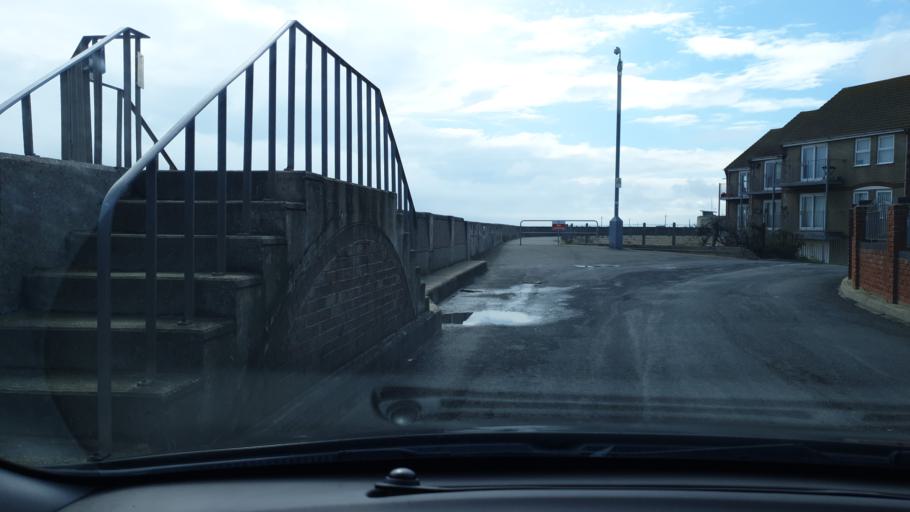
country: GB
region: England
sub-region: Essex
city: Saint Osyth
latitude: 51.7723
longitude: 1.0998
